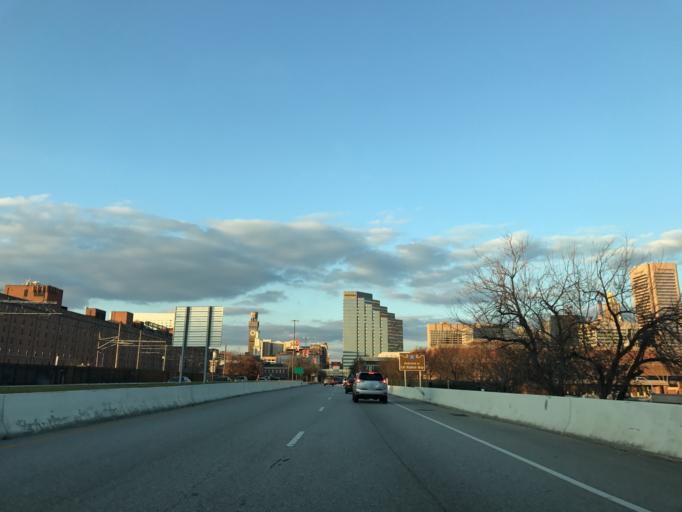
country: US
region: Maryland
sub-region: City of Baltimore
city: Baltimore
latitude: 39.2805
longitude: -76.6188
